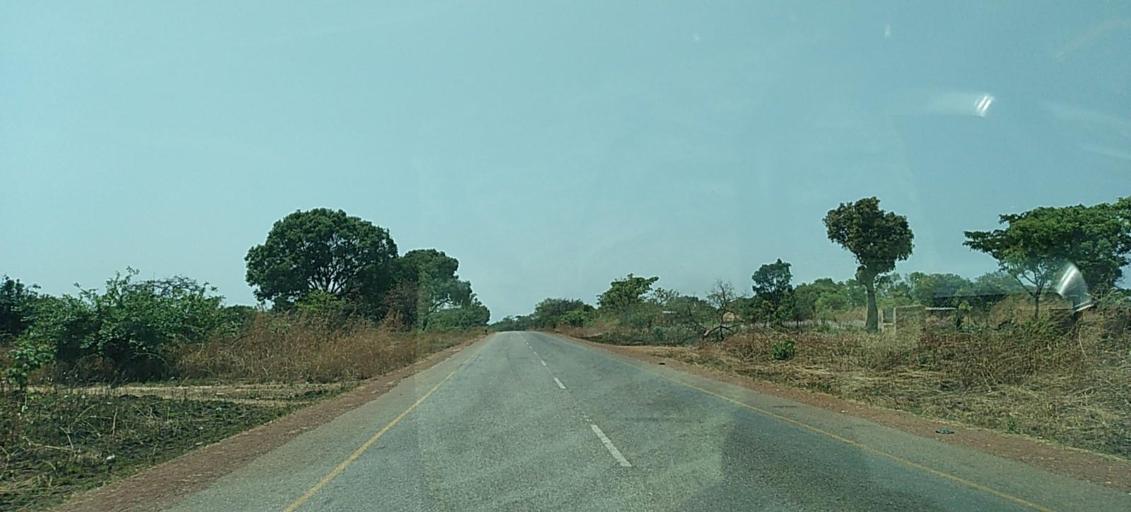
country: ZM
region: North-Western
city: Solwezi
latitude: -12.3899
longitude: 26.2069
